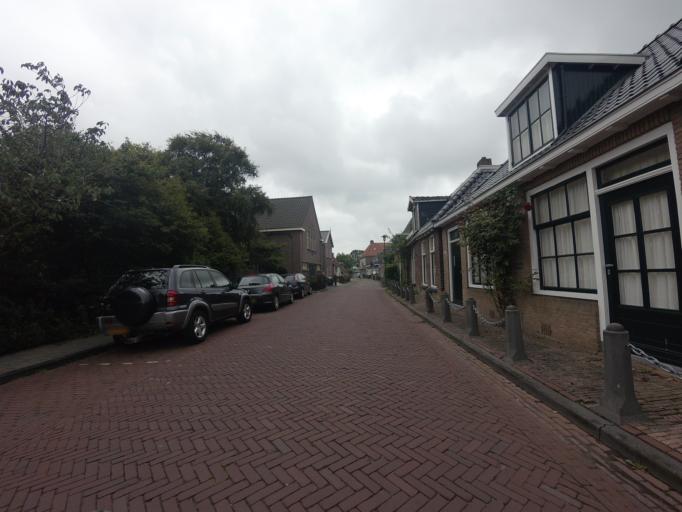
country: NL
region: Friesland
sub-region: Sudwest Fryslan
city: Heeg
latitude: 52.9930
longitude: 5.5483
